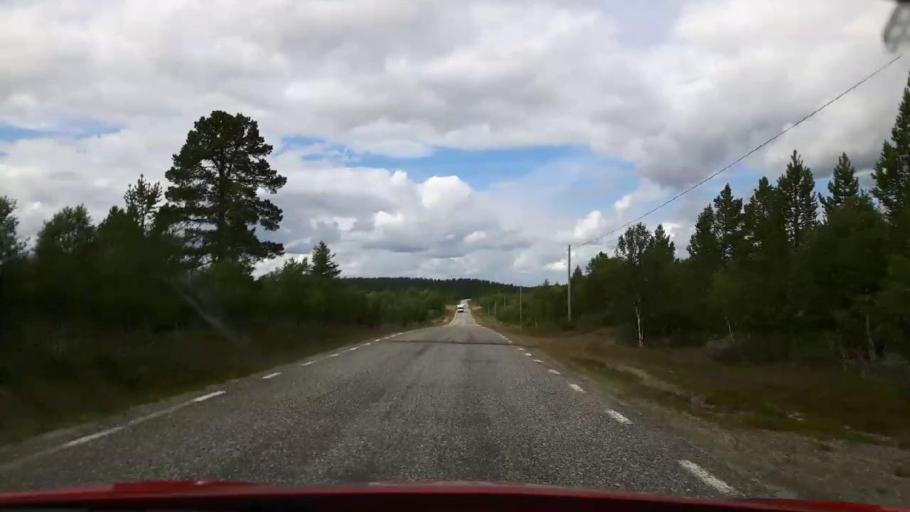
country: NO
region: Hedmark
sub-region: Engerdal
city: Engerdal
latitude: 62.2919
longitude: 12.8159
